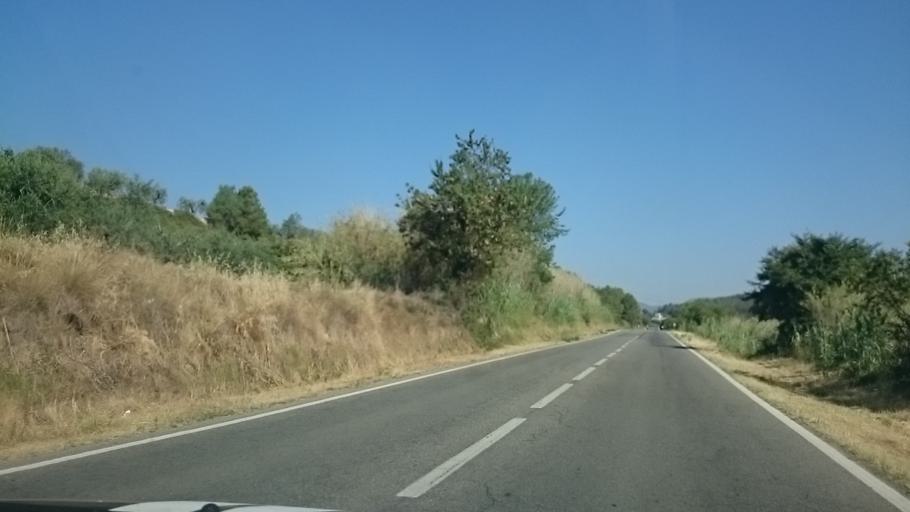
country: ES
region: Catalonia
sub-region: Provincia de Barcelona
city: Vilobi del Penedes
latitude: 41.3754
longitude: 1.6461
